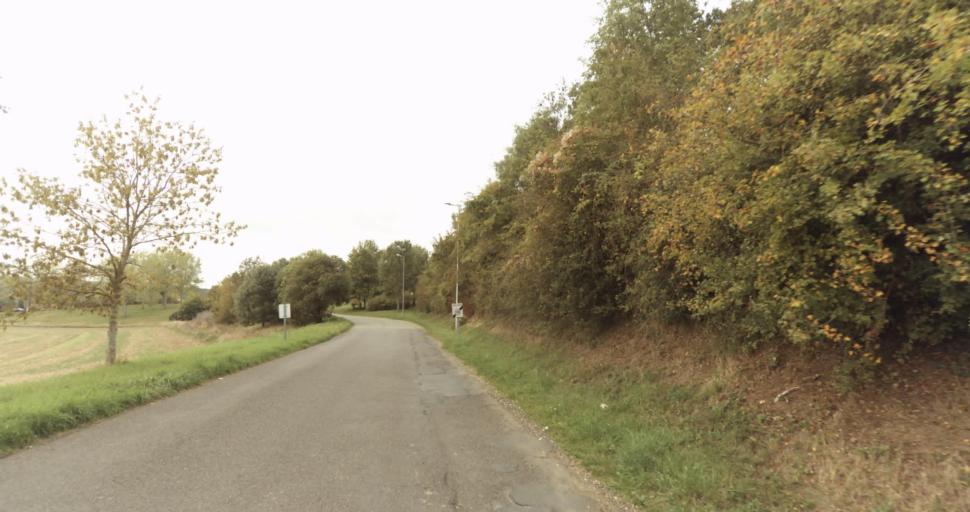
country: FR
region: Centre
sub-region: Departement d'Eure-et-Loir
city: Garnay
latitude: 48.7216
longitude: 1.3488
